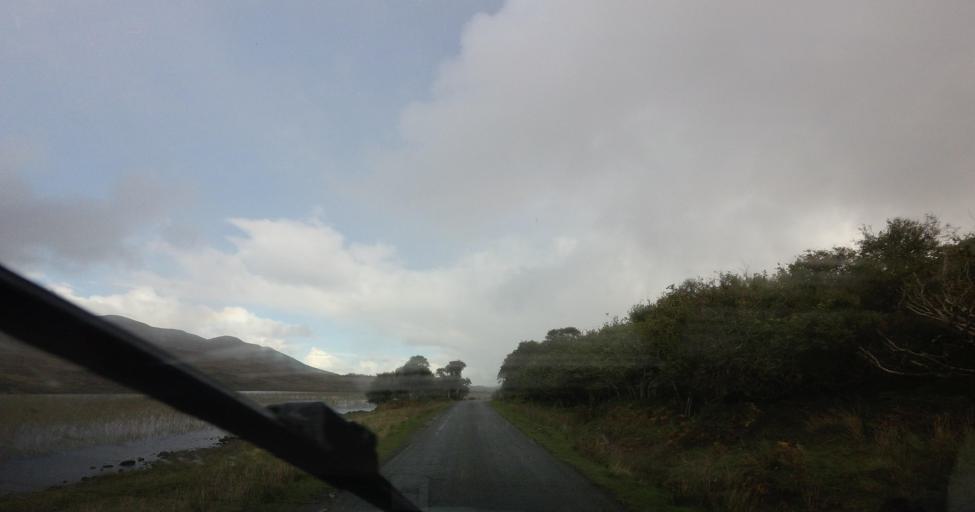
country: GB
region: Scotland
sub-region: Highland
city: Portree
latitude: 57.2094
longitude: -5.9657
